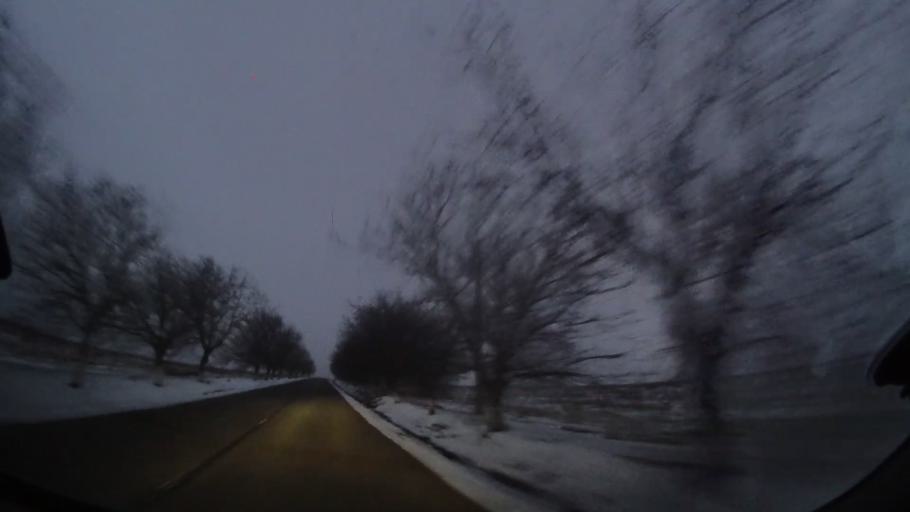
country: RO
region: Vaslui
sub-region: Comuna Hoceni
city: Hoceni
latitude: 46.5209
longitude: 28.0268
